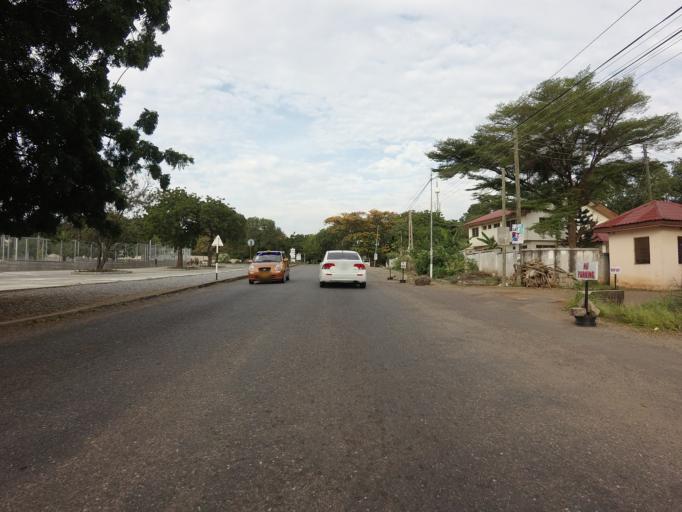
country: GH
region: Greater Accra
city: Accra
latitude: 5.5783
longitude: -0.1698
